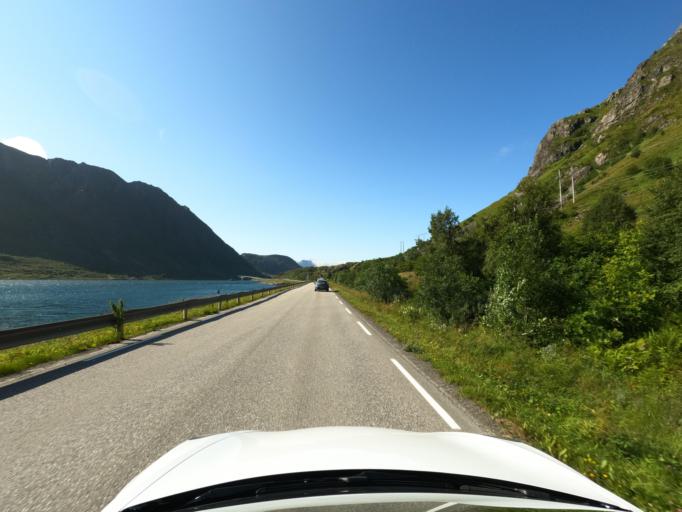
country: NO
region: Nordland
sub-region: Vagan
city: Kabelvag
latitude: 68.2640
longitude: 14.1820
